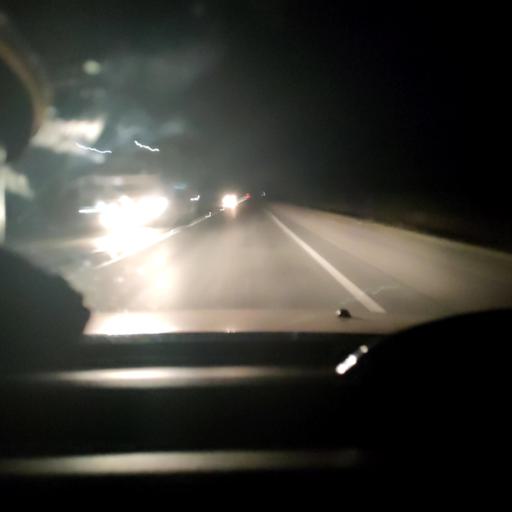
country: RU
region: Samara
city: Chapayevsk
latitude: 52.9902
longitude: 49.8466
